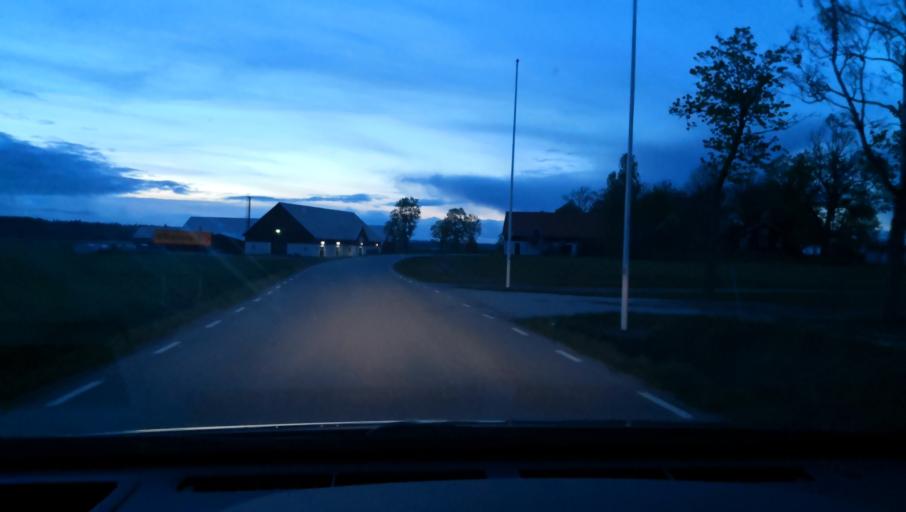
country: SE
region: OErebro
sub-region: Orebro Kommun
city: Vintrosa
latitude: 59.1338
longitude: 14.9990
